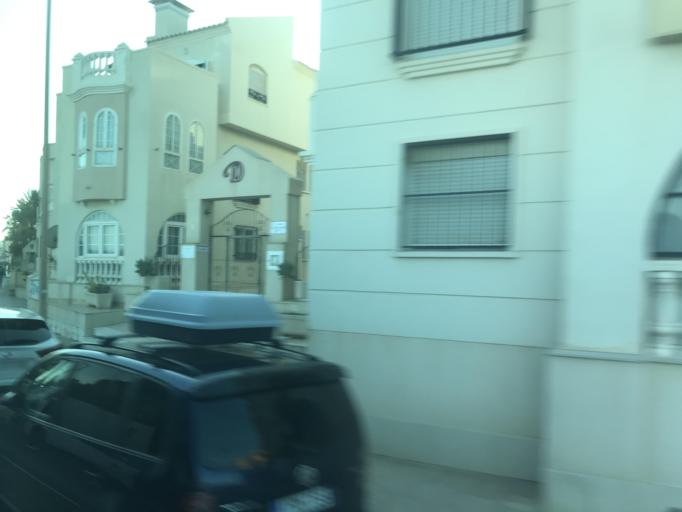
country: ES
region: Valencia
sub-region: Provincia de Alicante
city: Torrevieja
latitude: 37.9855
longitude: -0.6576
